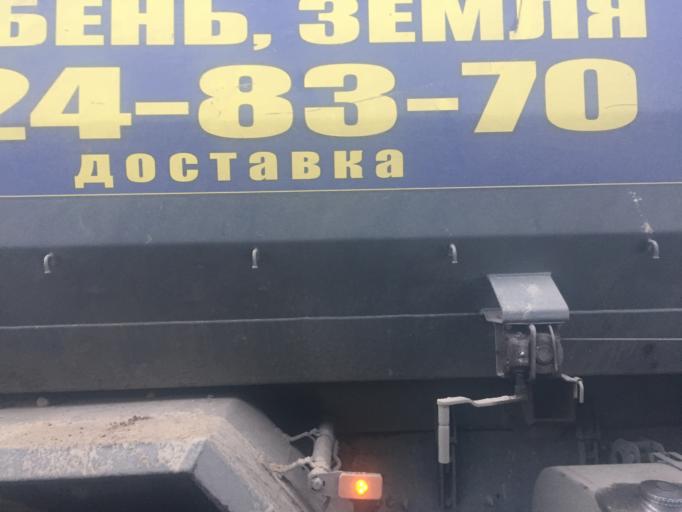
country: RU
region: St.-Petersburg
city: Obukhovo
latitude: 59.8851
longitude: 30.4664
